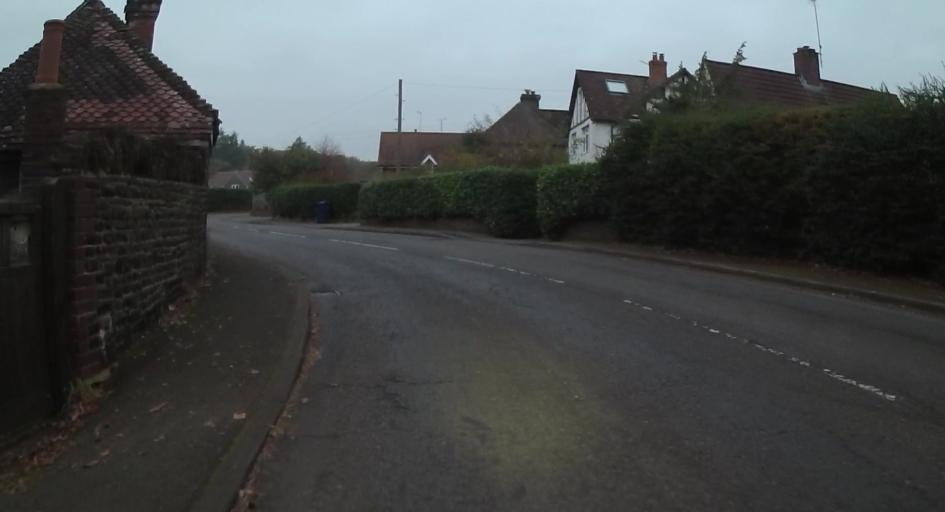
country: GB
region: England
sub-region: Surrey
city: Elstead
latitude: 51.1866
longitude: -0.7475
